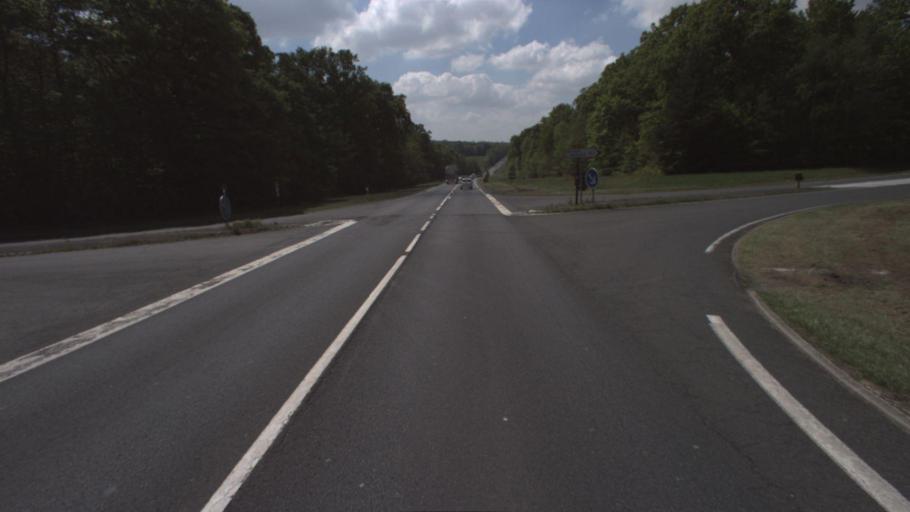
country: FR
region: Ile-de-France
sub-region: Departement de Seine-et-Marne
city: Chaumes-en-Brie
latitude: 48.6649
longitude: 2.8106
